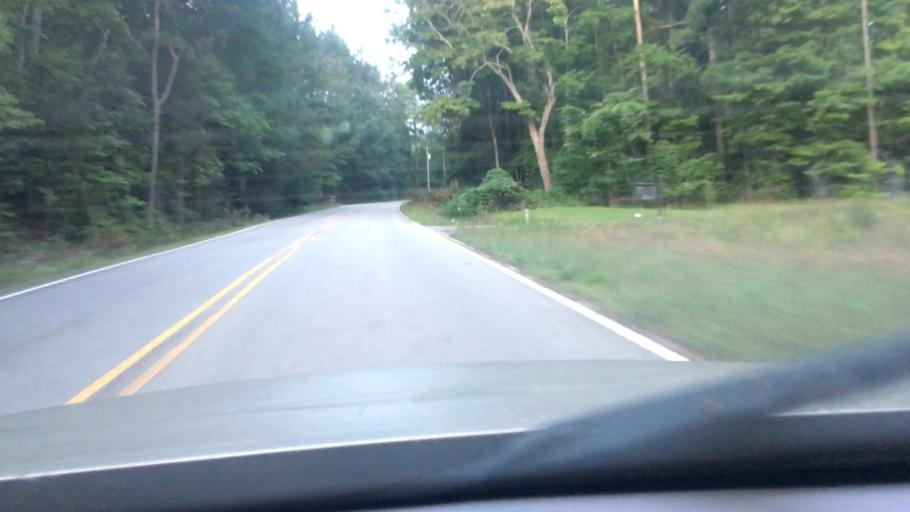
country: US
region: South Carolina
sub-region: Lexington County
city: Irmo
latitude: 34.1372
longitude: -81.1843
